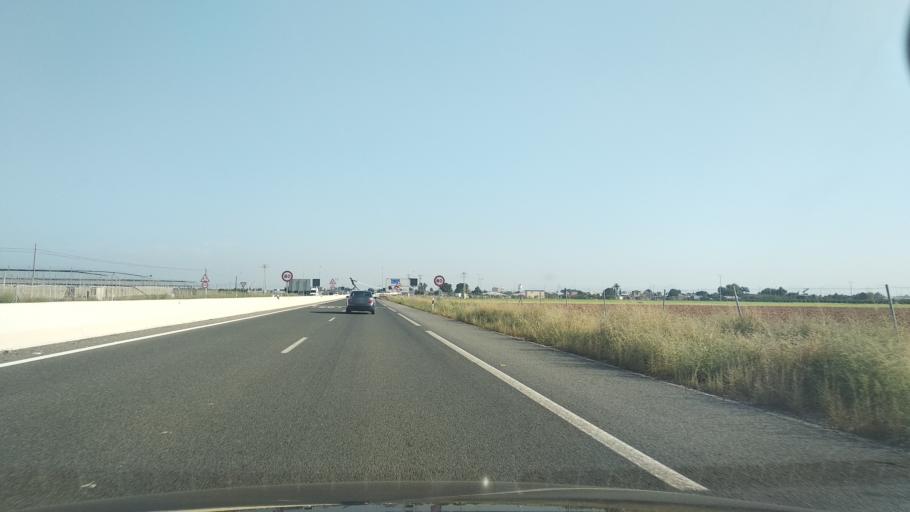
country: ES
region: Murcia
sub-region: Murcia
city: San Javier
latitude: 37.8240
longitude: -0.8521
